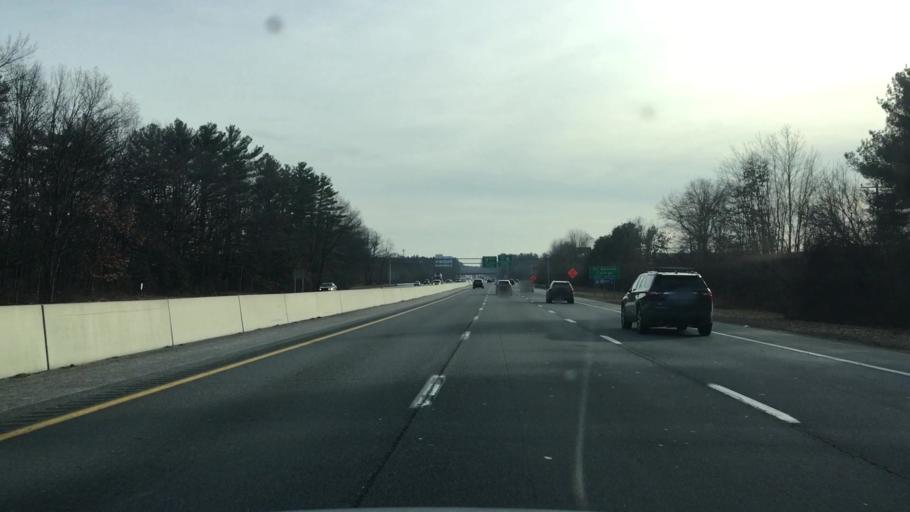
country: US
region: New Hampshire
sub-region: Hillsborough County
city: Manchester
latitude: 42.9600
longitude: -71.4754
